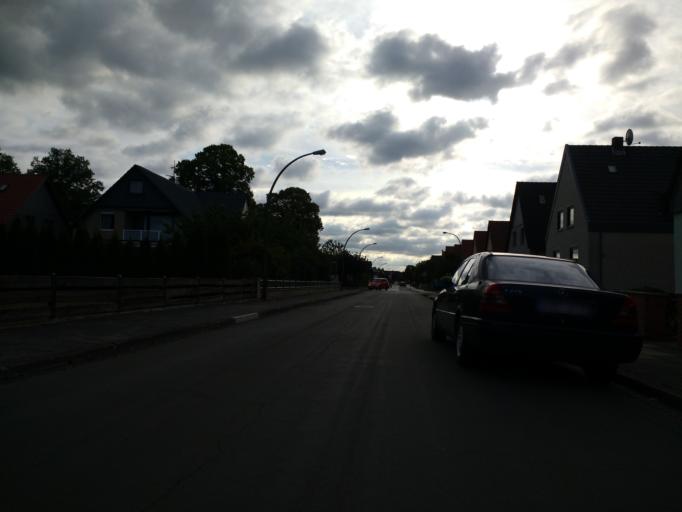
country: DE
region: Lower Saxony
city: Weyhausen
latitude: 52.4207
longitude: 10.6993
